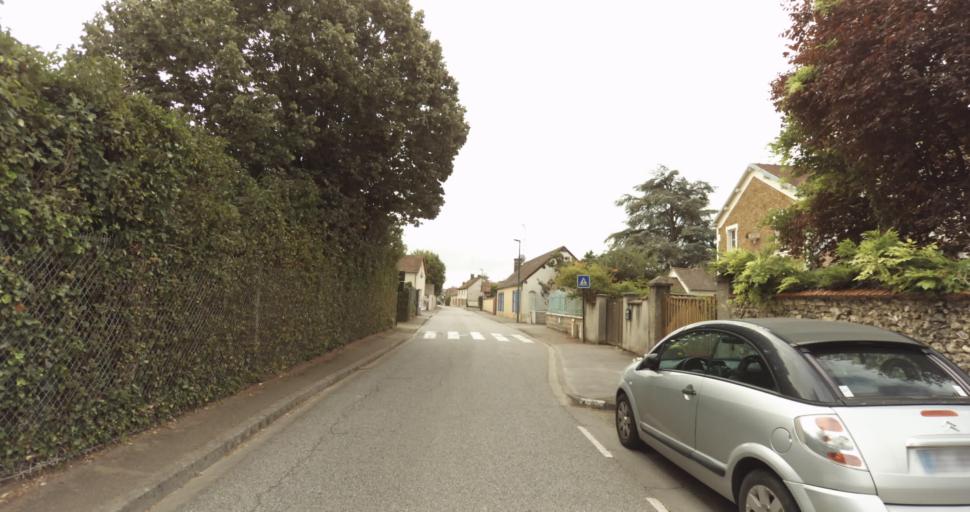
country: FR
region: Haute-Normandie
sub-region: Departement de l'Eure
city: Garennes-sur-Eure
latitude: 48.9132
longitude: 1.4359
